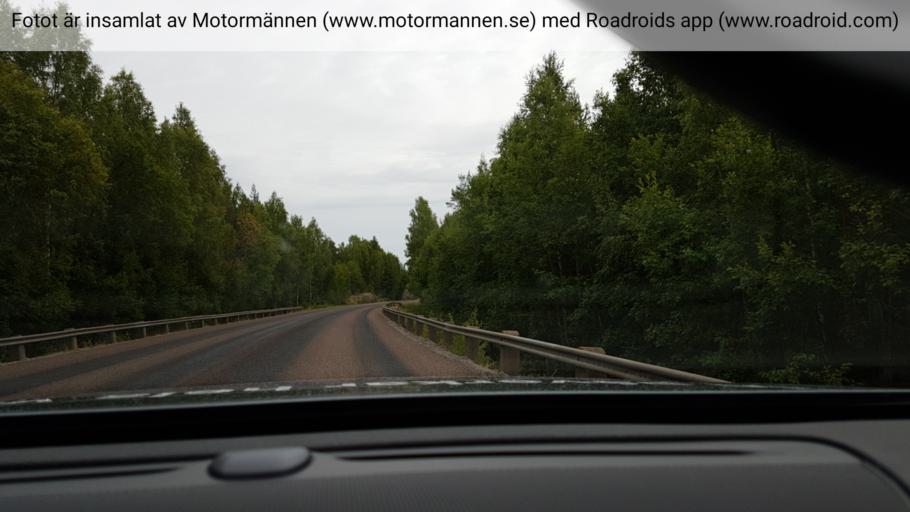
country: SE
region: Dalarna
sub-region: Ludvika Kommun
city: Ludvika
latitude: 60.2951
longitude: 15.2221
